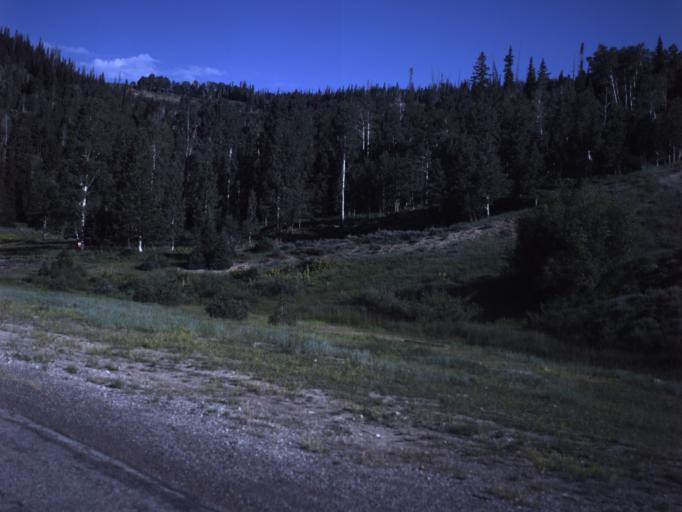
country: US
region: Utah
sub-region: Sanpete County
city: Fairview
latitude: 39.5873
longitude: -111.2412
